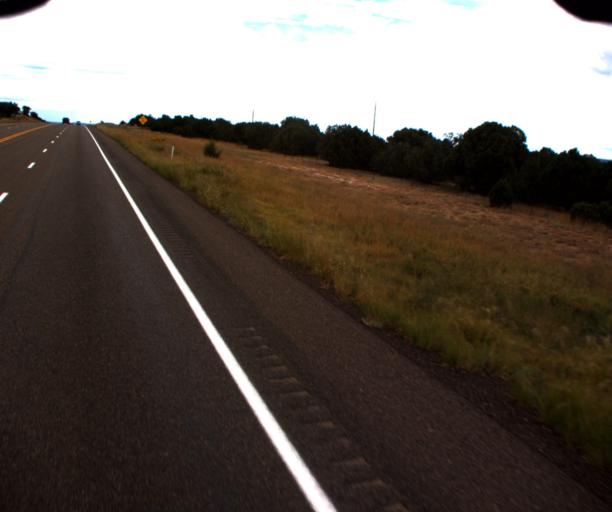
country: US
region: Arizona
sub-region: Navajo County
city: White Mountain Lake
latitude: 34.3362
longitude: -110.0491
